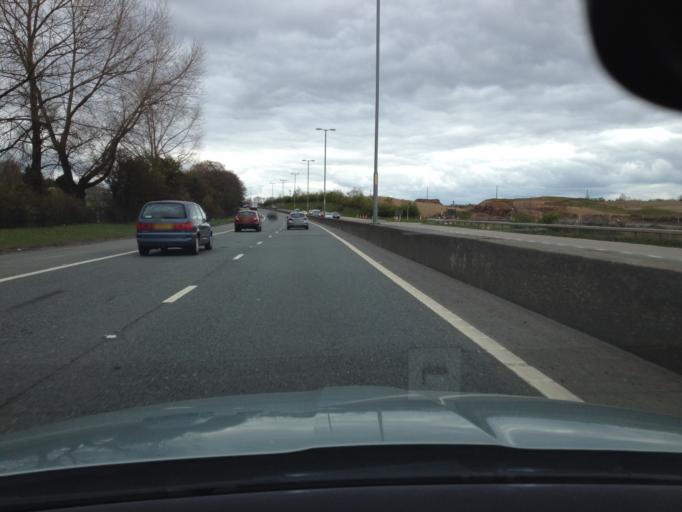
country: GB
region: Scotland
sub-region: North Lanarkshire
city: Coatbridge
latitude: 55.8453
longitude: -4.0561
